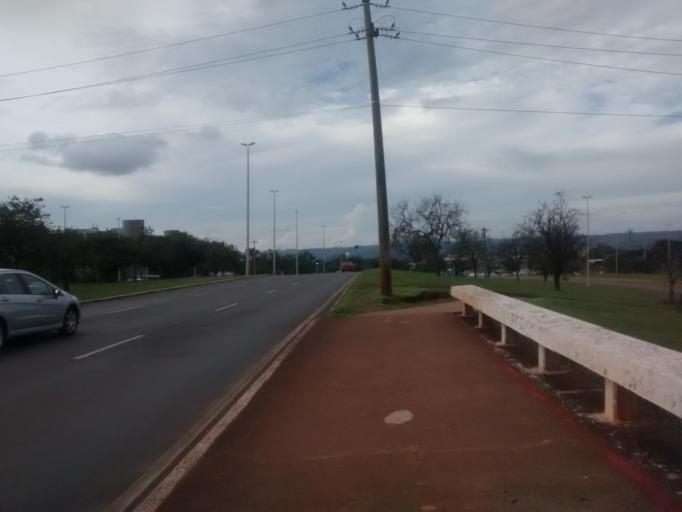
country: BR
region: Federal District
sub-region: Brasilia
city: Brasilia
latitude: -15.7933
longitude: -47.8748
